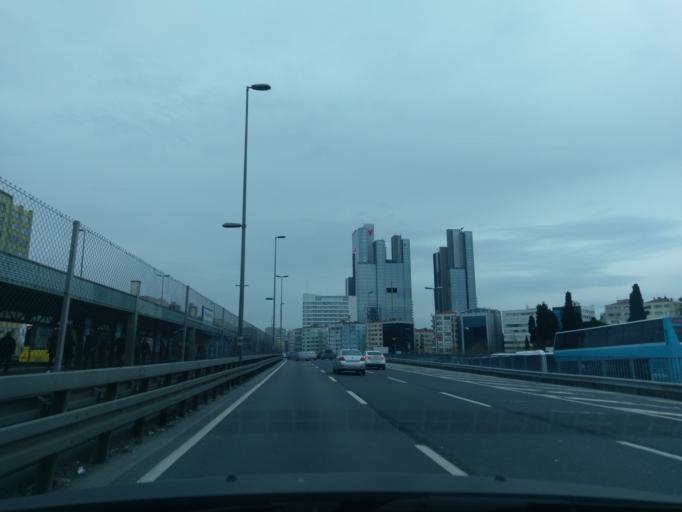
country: TR
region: Istanbul
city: Sisli
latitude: 41.0668
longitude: 28.9915
